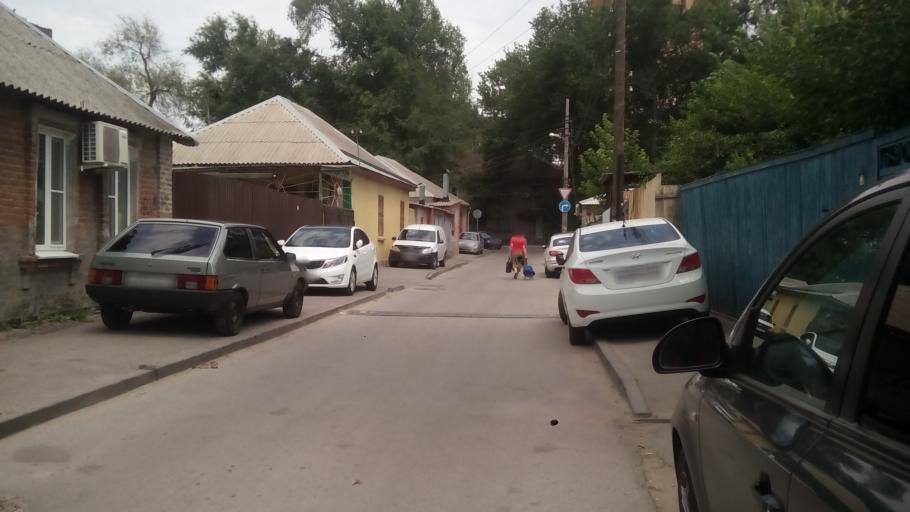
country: RU
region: Rostov
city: Rostov-na-Donu
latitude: 47.2481
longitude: 39.7416
